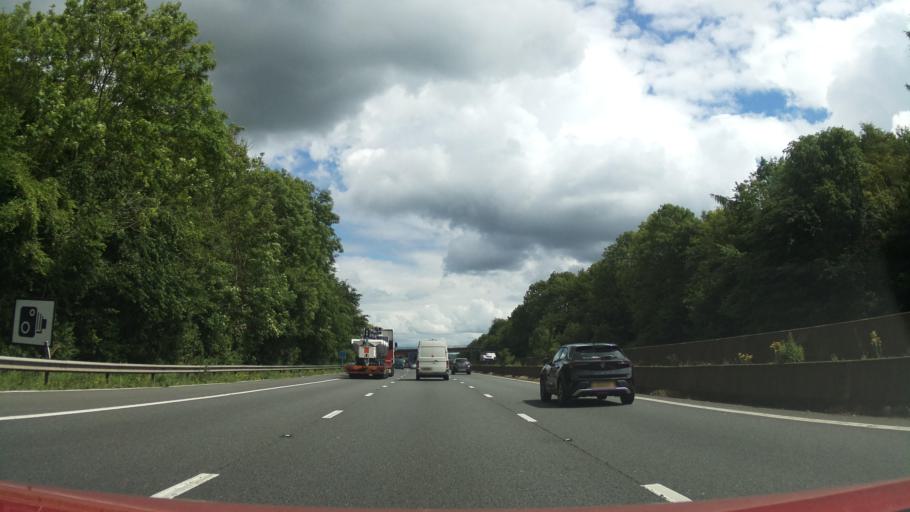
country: GB
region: England
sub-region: Borough of Swindon
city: Chiseldon
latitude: 51.5305
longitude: -1.7542
